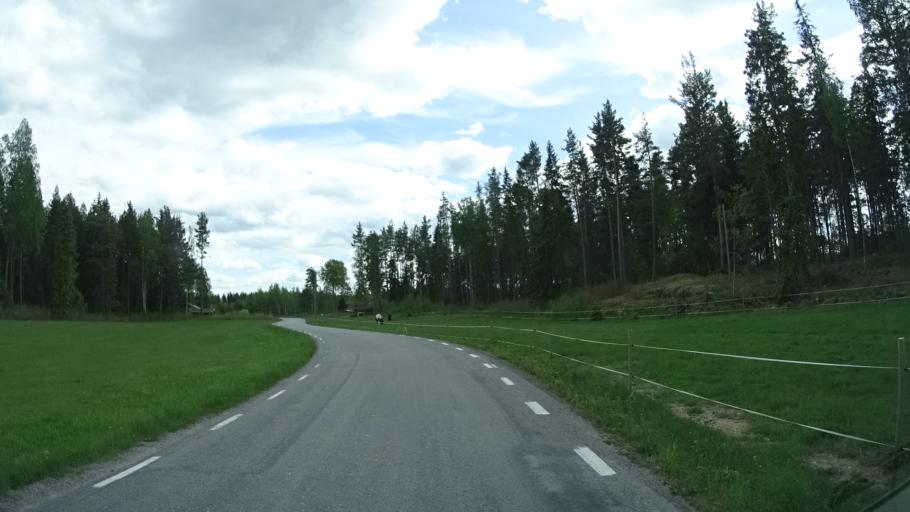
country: SE
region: OEstergoetland
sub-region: Finspangs Kommun
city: Finspang
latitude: 58.6030
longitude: 15.7567
